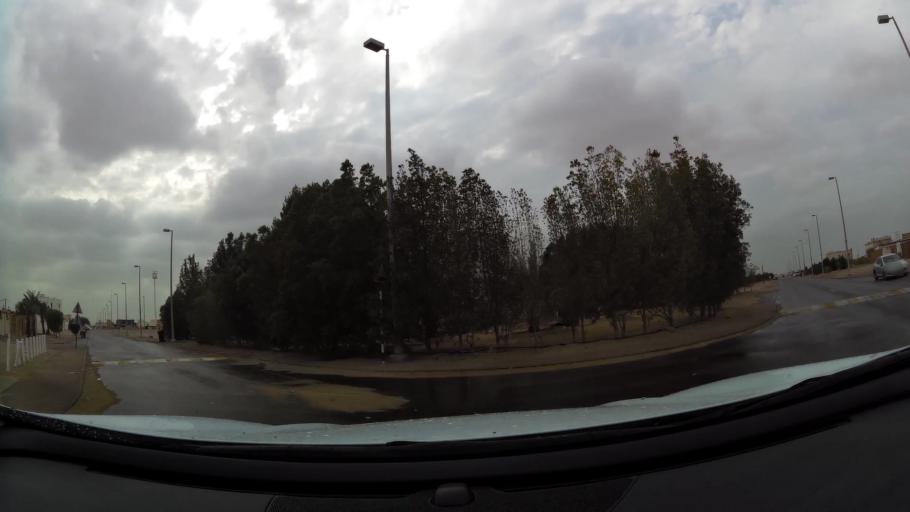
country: AE
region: Abu Dhabi
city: Abu Dhabi
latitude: 24.3608
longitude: 54.6218
